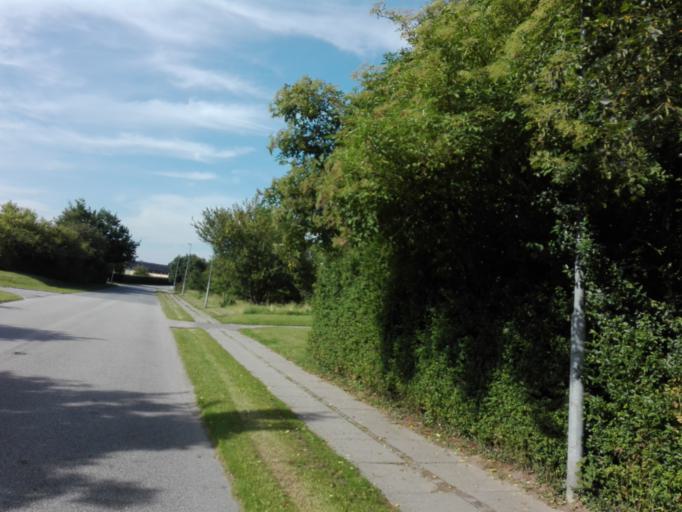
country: DK
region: Central Jutland
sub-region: Arhus Kommune
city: Tranbjerg
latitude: 56.0972
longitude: 10.1299
